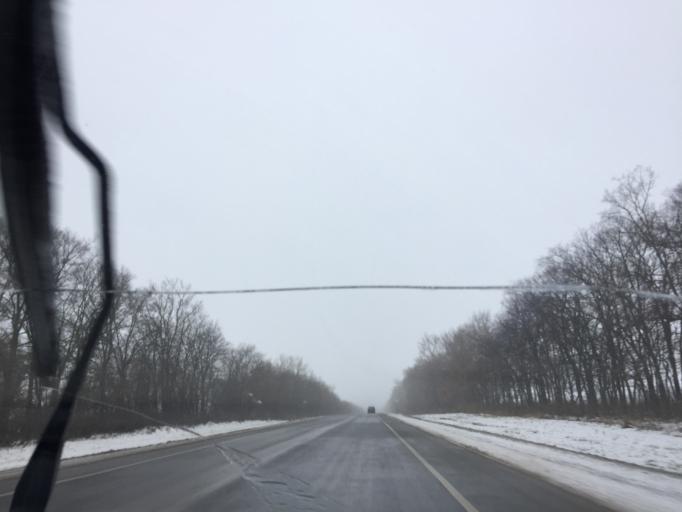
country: RU
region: Tula
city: Plavsk
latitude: 53.8059
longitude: 37.3851
